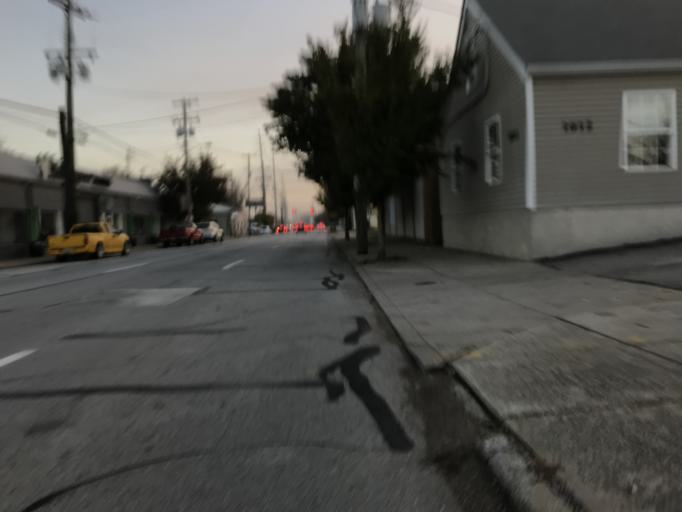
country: US
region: Indiana
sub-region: Clark County
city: Jeffersonville
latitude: 38.2567
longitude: -85.7207
